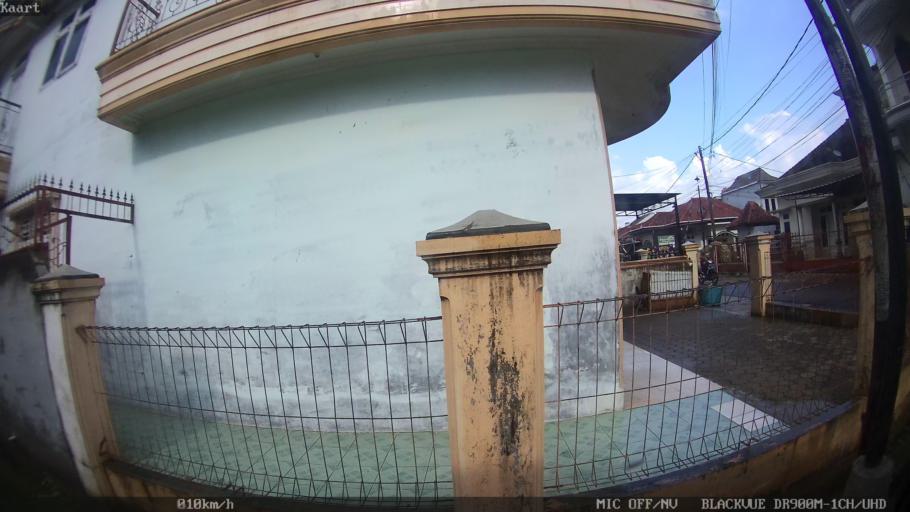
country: ID
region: Lampung
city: Kedaton
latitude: -5.3874
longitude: 105.2997
